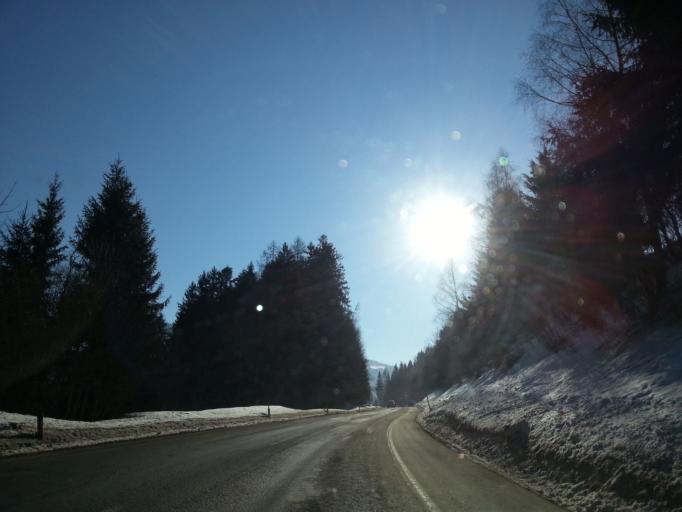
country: AT
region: Salzburg
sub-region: Politischer Bezirk Sankt Johann im Pongau
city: Eben im Pongau
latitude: 47.4175
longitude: 13.3794
